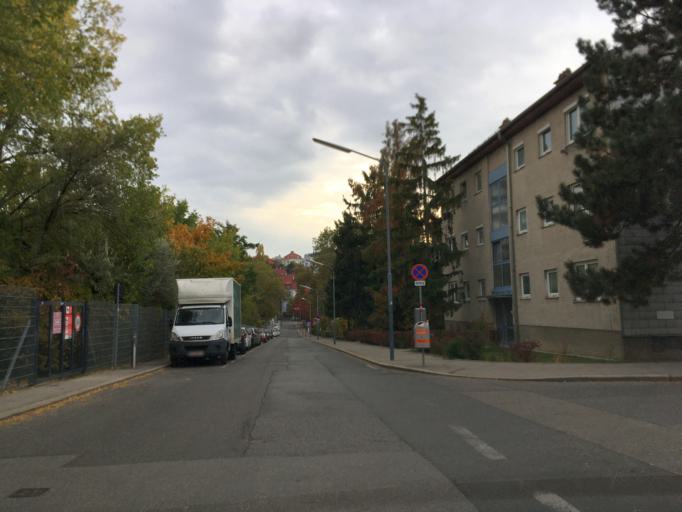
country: AT
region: Vienna
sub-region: Wien Stadt
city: Vienna
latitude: 48.2445
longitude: 16.3254
